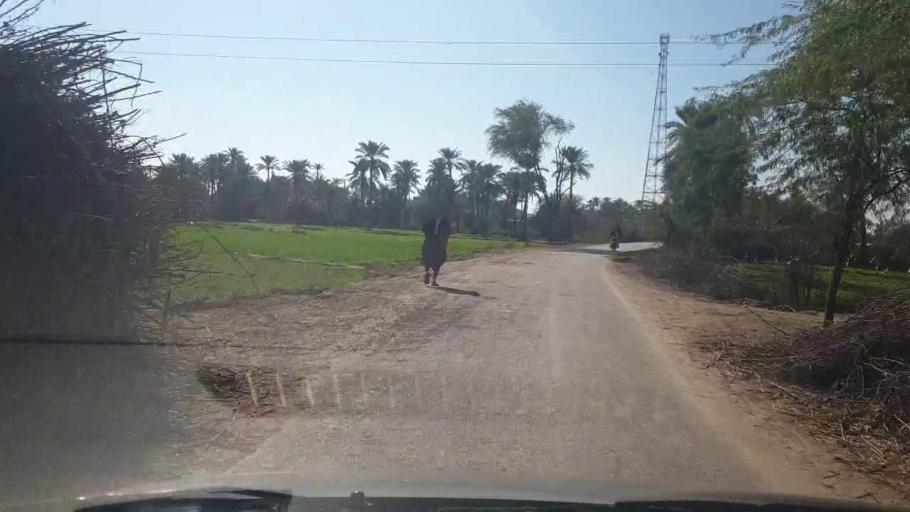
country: PK
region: Sindh
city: Bozdar
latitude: 27.1460
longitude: 68.6480
